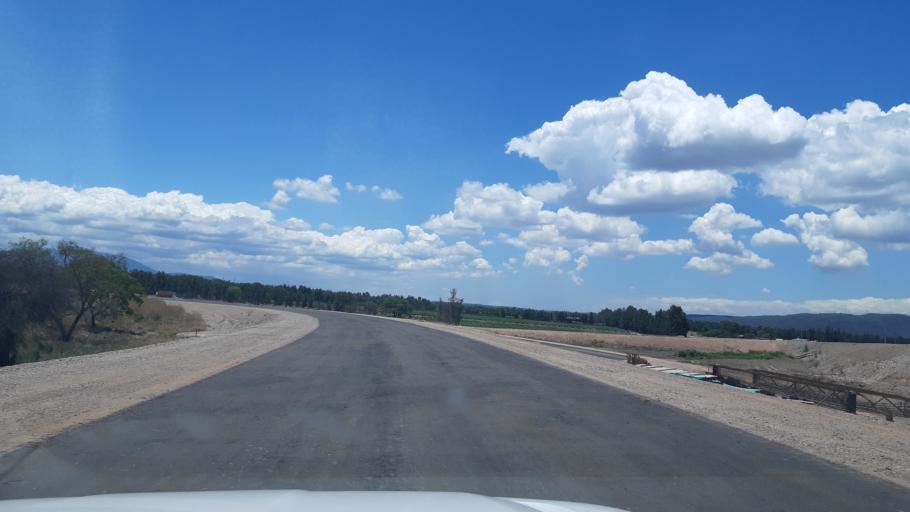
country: AR
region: Jujuy
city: La Mendieta
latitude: -24.4769
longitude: -65.0387
